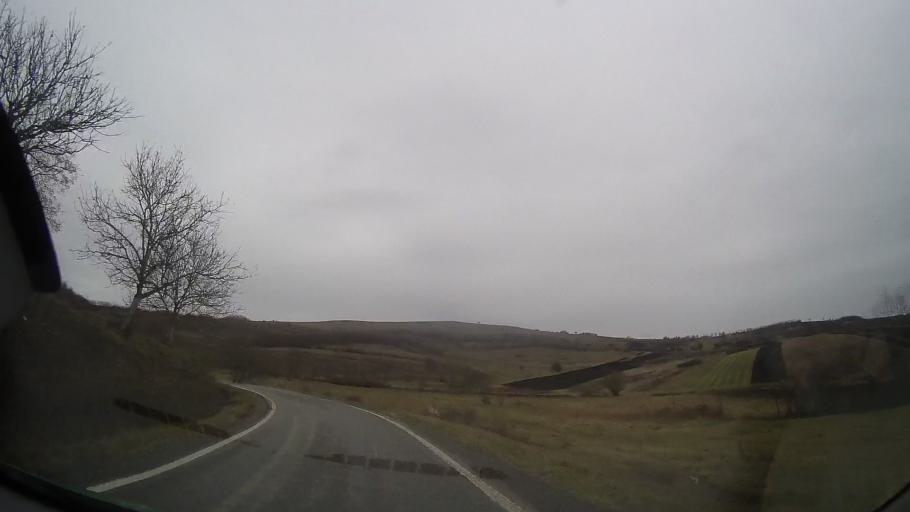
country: RO
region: Mures
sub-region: Comuna Bala
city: Bala
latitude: 46.7145
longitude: 24.5257
